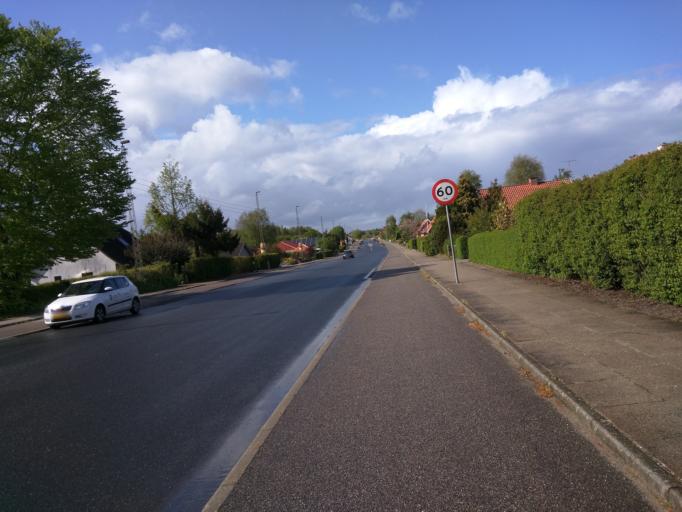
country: DK
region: Central Jutland
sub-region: Viborg Kommune
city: Viborg
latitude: 56.4251
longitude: 9.4036
